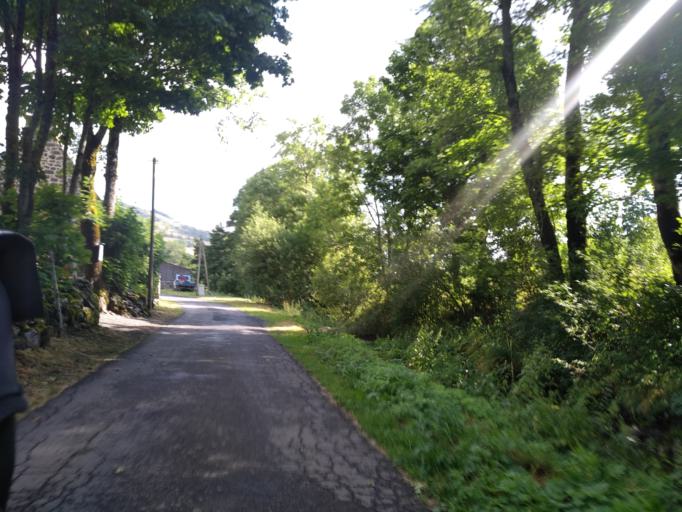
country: FR
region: Auvergne
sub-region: Departement du Cantal
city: Murat
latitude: 45.1302
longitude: 2.7435
